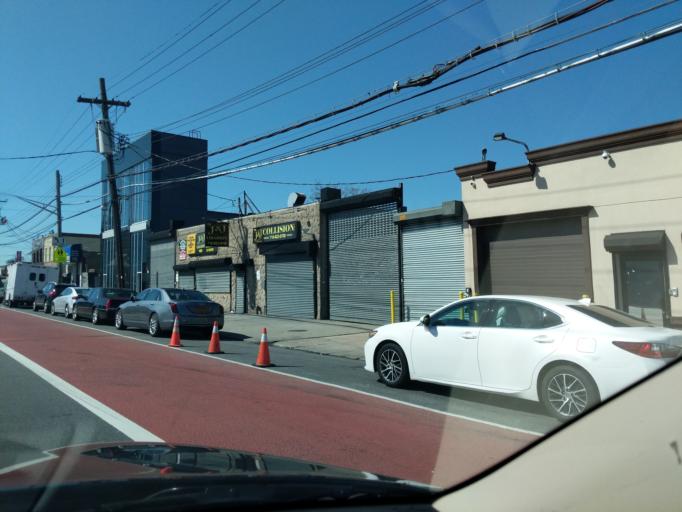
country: US
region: New York
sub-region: Kings County
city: Brooklyn
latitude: 40.6331
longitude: -73.9282
